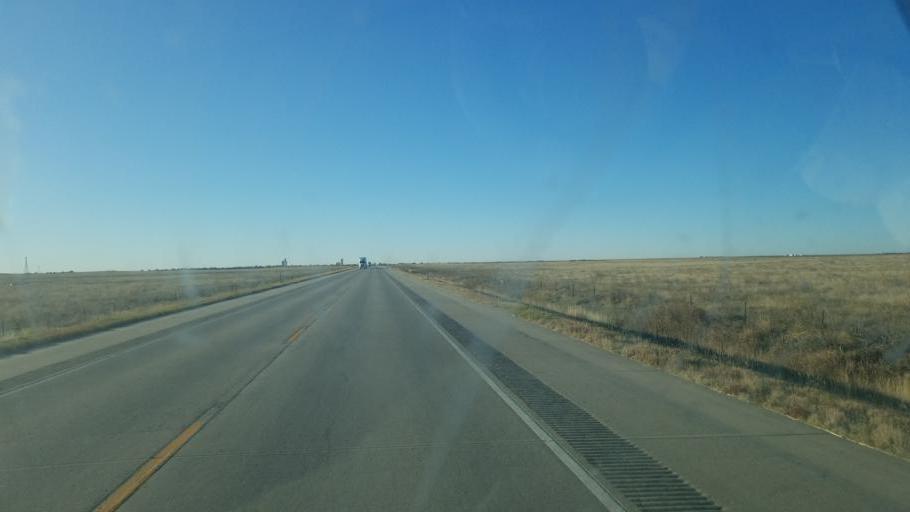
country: US
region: Colorado
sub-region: Kiowa County
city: Eads
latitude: 38.5147
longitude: -102.7857
